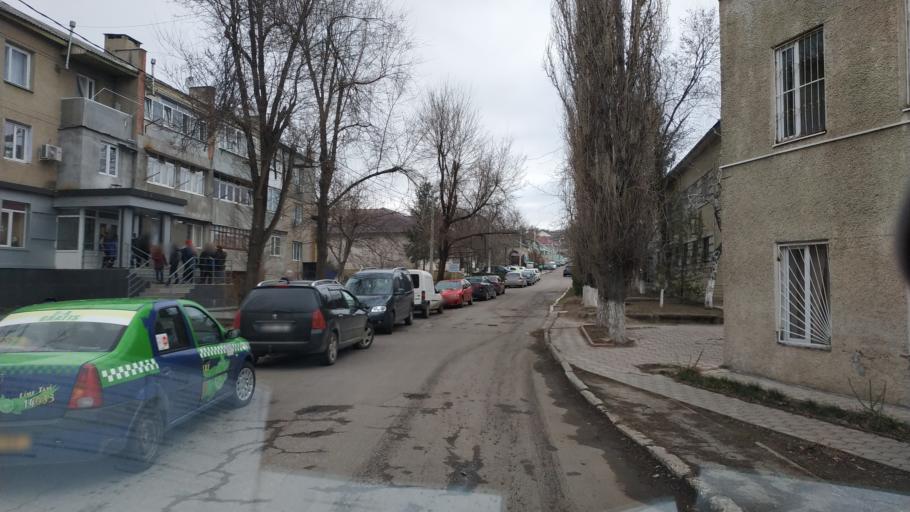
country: MD
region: Causeni
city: Causeni
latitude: 46.6417
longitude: 29.4116
